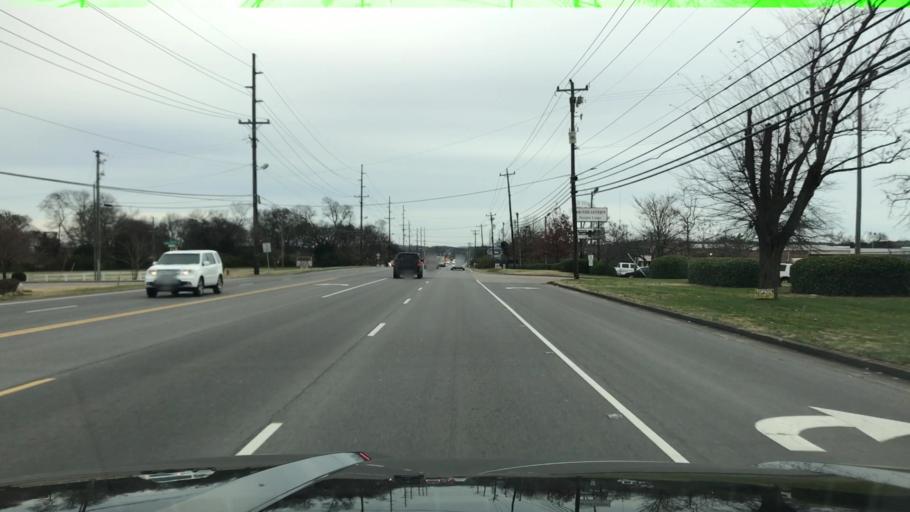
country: US
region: Tennessee
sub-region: Rutherford County
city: La Vergne
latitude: 36.0321
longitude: -86.5947
